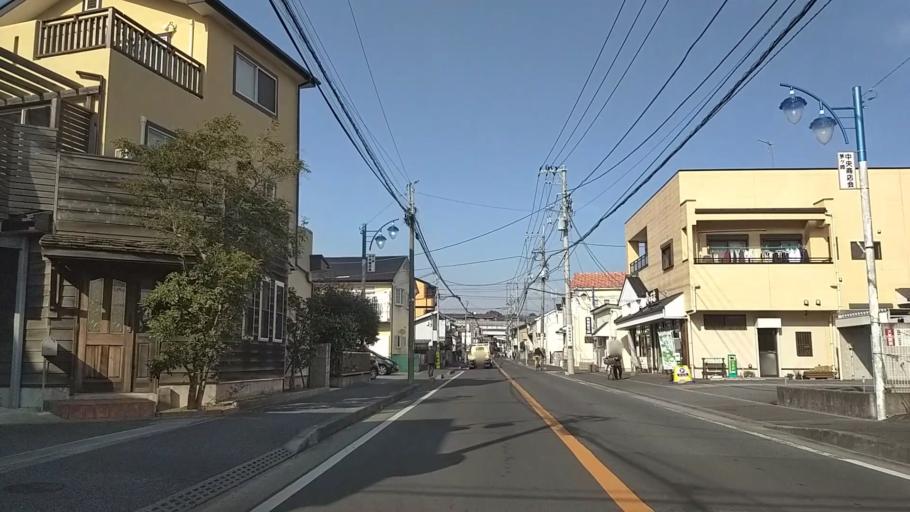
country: JP
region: Kanagawa
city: Chigasaki
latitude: 35.3476
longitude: 139.4135
